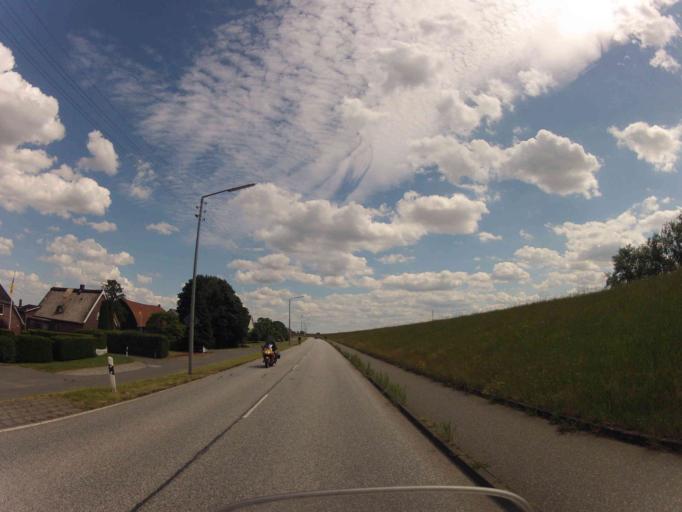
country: DE
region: Hamburg
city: Rothenburgsort
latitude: 53.4602
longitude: 10.0700
